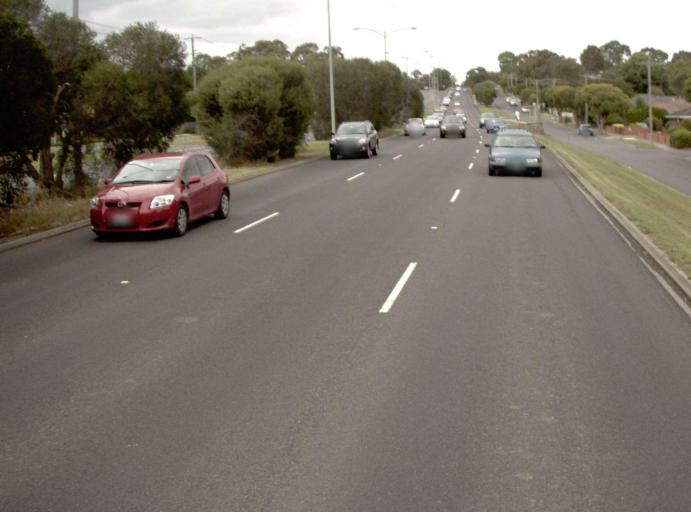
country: AU
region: Victoria
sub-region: Maroondah
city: Croydon North
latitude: -37.7734
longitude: 145.2931
